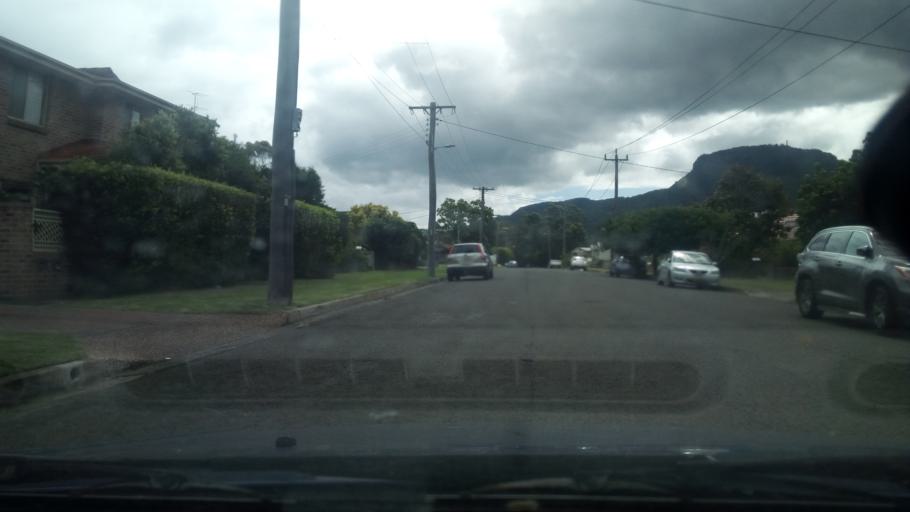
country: AU
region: New South Wales
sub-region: Wollongong
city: Gwynneville
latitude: -34.4143
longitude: 150.8855
